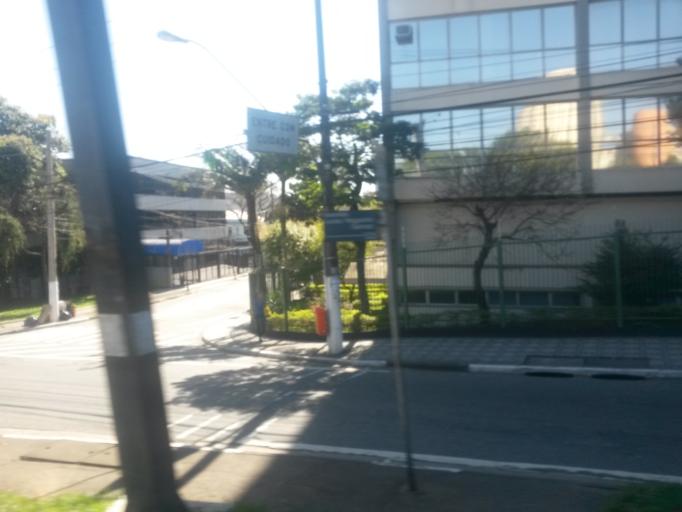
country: BR
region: Sao Paulo
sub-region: Sao Bernardo Do Campo
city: Sao Bernardo do Campo
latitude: -23.6902
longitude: -46.5594
